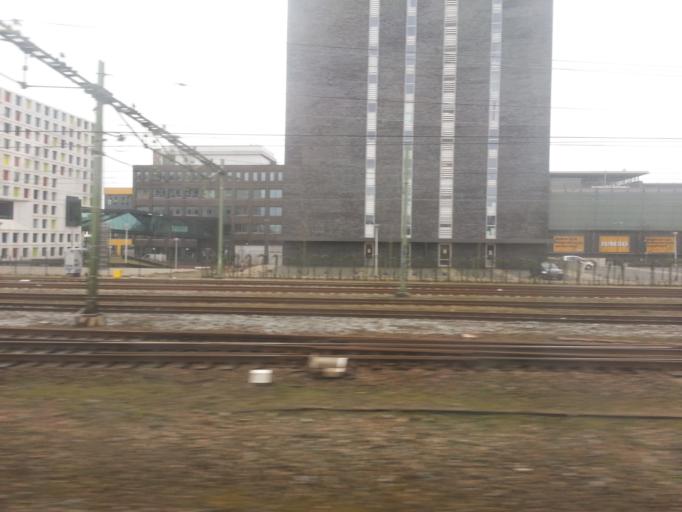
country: NL
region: South Holland
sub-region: Gemeente Den Haag
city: The Hague
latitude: 52.0678
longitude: 4.3181
